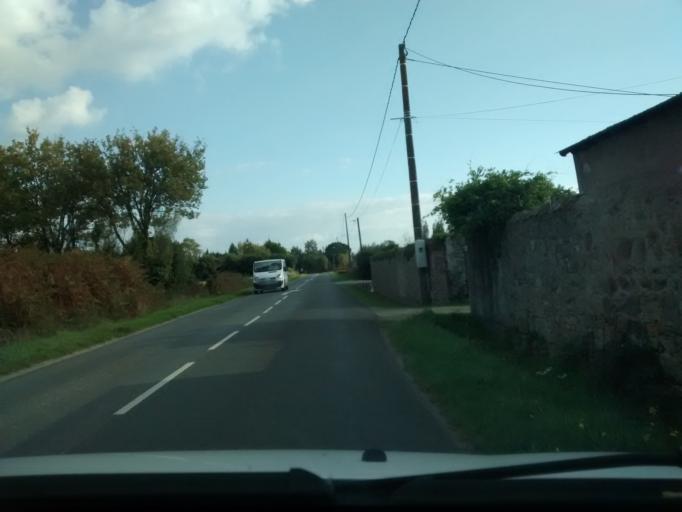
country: FR
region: Pays de la Loire
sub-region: Departement de la Loire-Atlantique
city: Sautron
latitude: 47.2881
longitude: -1.6557
